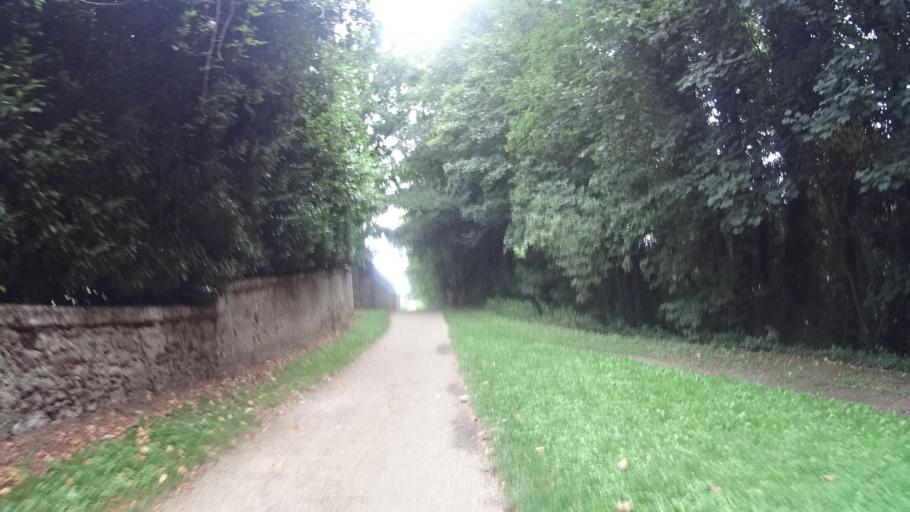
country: FR
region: Centre
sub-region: Departement du Loir-et-Cher
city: Saint-Claude-de-Diray
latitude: 47.6390
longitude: 1.4133
